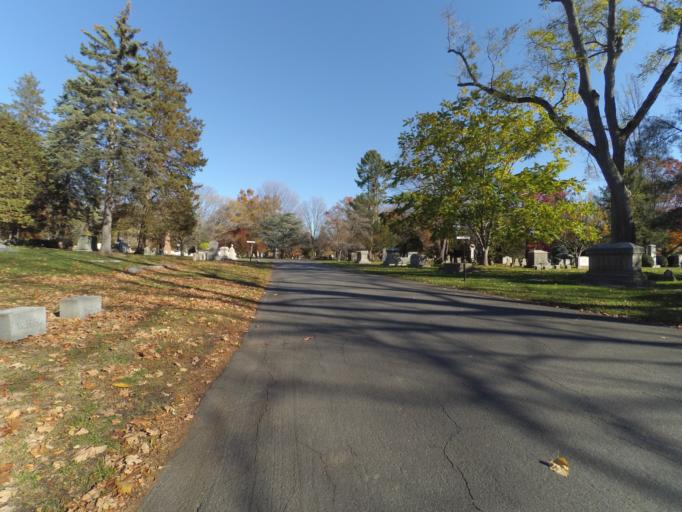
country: US
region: Massachusetts
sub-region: Middlesex County
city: Watertown
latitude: 42.3672
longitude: -71.1450
